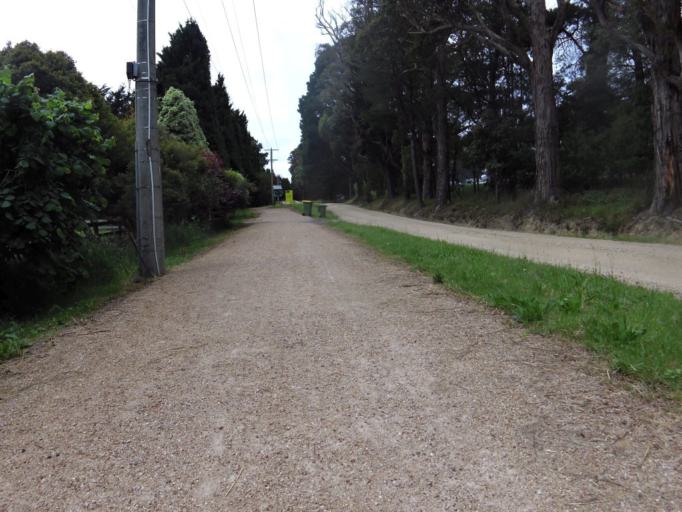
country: AU
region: Victoria
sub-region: Cardinia
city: Cockatoo
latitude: -37.9450
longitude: 145.5102
